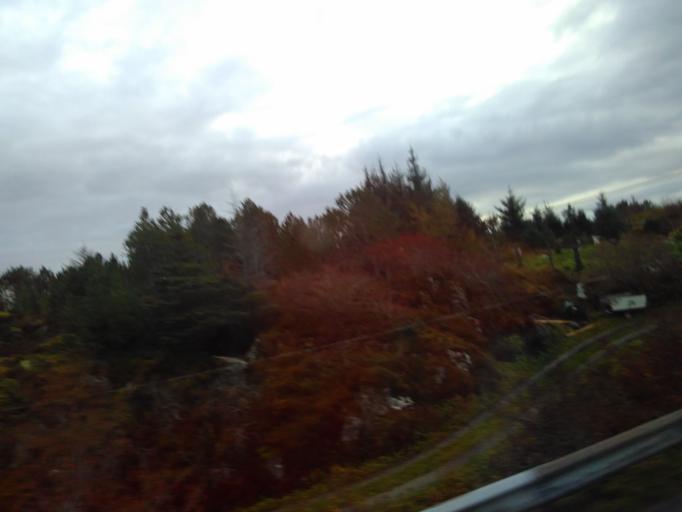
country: NO
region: Sor-Trondelag
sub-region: Froya
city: Sistranda
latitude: 63.7457
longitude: 8.8374
